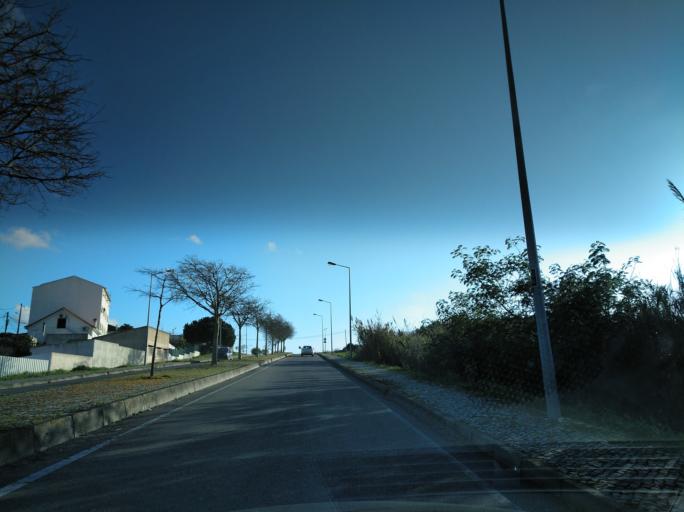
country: PT
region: Setubal
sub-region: Almada
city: Sobreda
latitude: 38.6573
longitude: -9.1885
